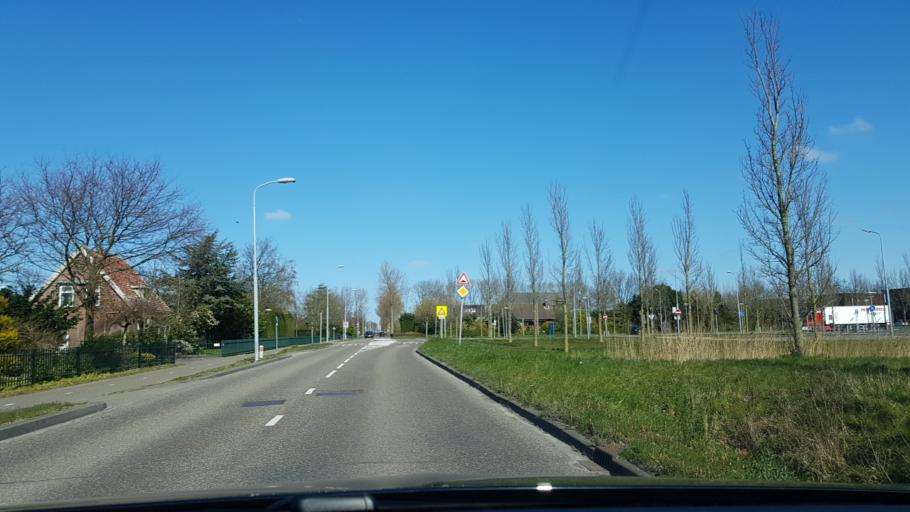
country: NL
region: South Holland
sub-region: Gemeente Hillegom
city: Hillegom
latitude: 52.2812
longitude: 4.6179
